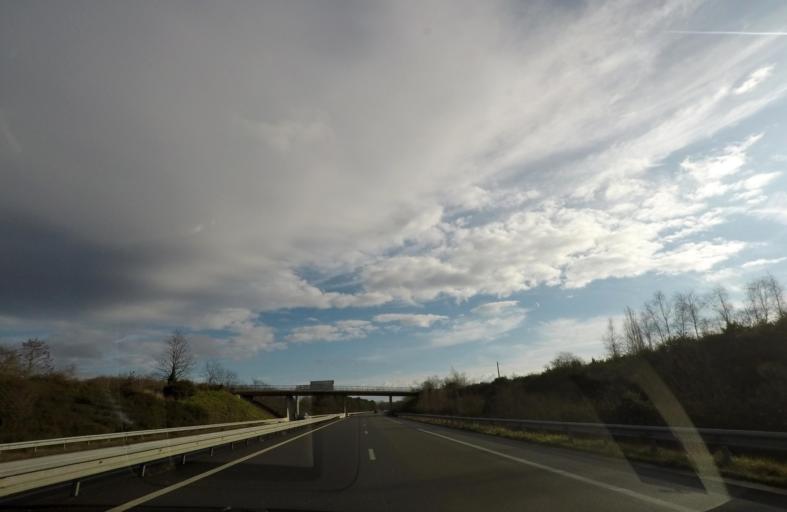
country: FR
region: Centre
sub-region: Departement du Loir-et-Cher
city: Chatres-sur-Cher
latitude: 47.3086
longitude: 1.8432
